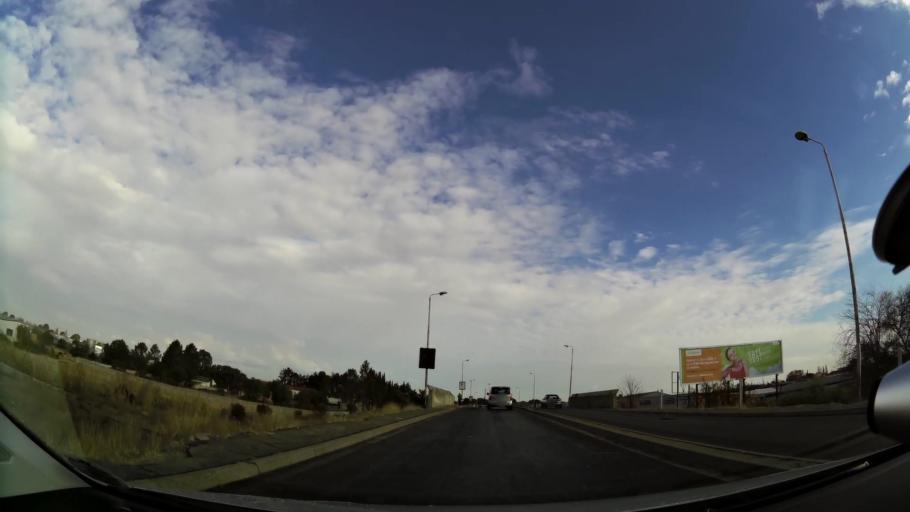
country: ZA
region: Orange Free State
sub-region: Lejweleputswa District Municipality
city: Welkom
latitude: -27.9772
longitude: 26.7622
